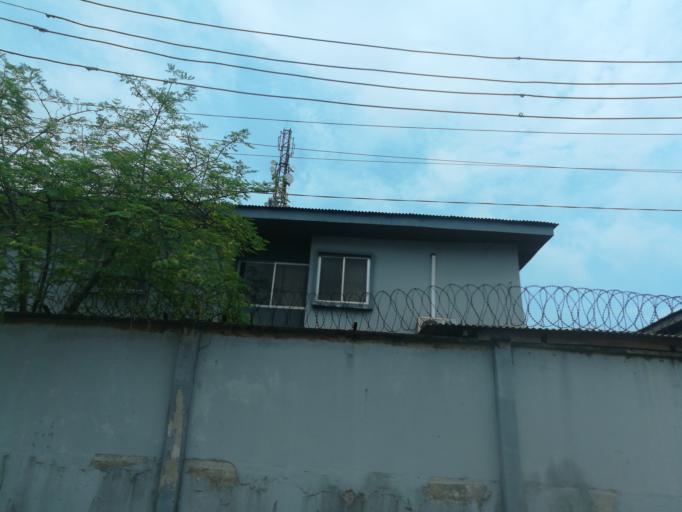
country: NG
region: Lagos
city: Ojota
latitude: 6.5870
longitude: 3.3648
